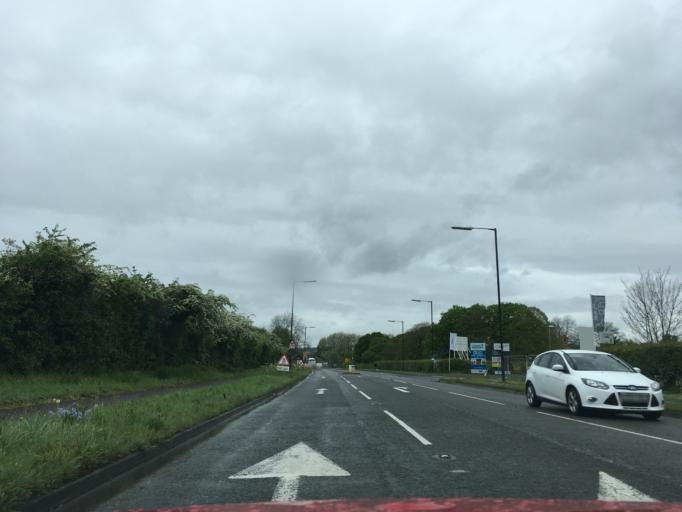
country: GB
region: England
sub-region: North Somerset
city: Hutton
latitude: 51.3343
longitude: -2.9055
